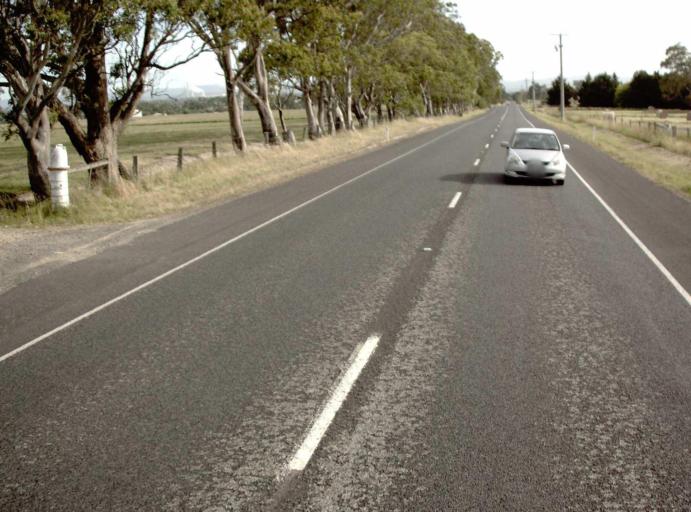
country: AU
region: Victoria
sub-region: Latrobe
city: Traralgon
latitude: -38.1421
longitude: 146.5563
